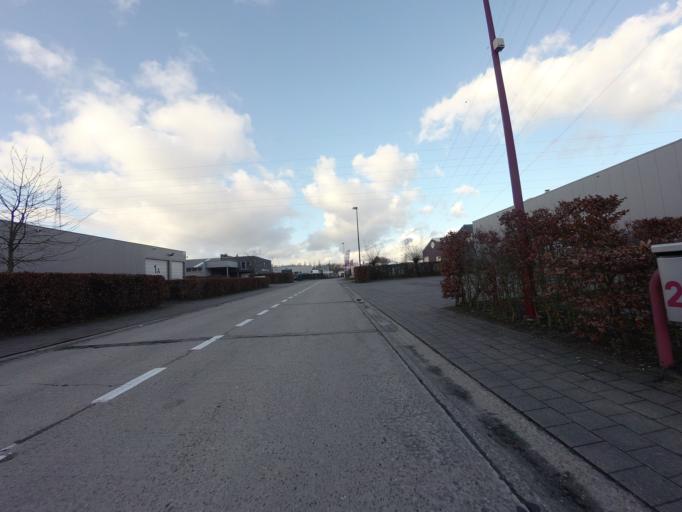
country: BE
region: Flanders
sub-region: Provincie Antwerpen
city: Lint
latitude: 51.1269
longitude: 4.5160
